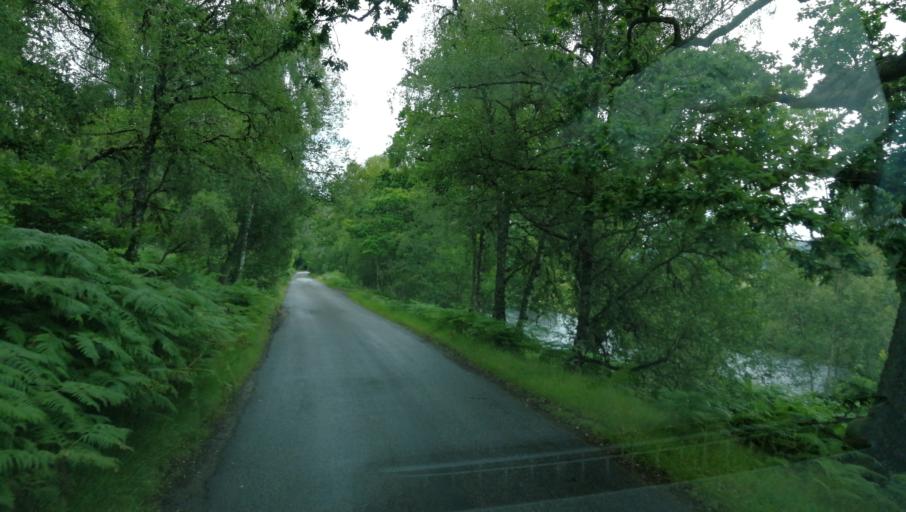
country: GB
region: Scotland
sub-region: Highland
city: Beauly
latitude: 57.3273
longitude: -4.7935
